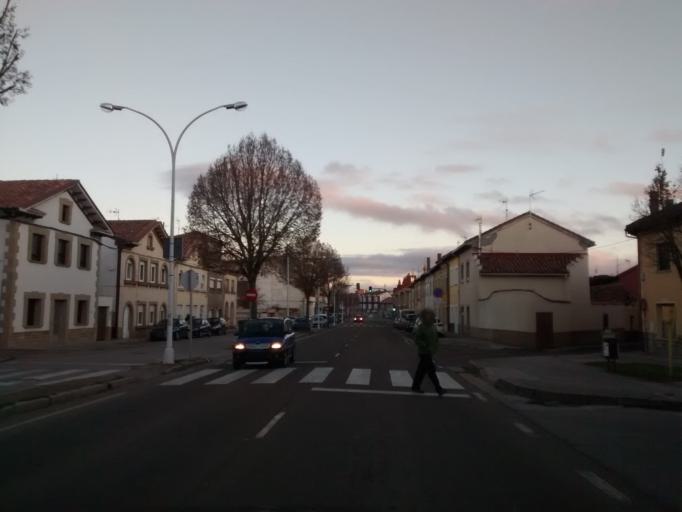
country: ES
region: Castille and Leon
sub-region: Provincia de Palencia
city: Aguilar de Campoo
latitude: 42.7948
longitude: -4.2593
